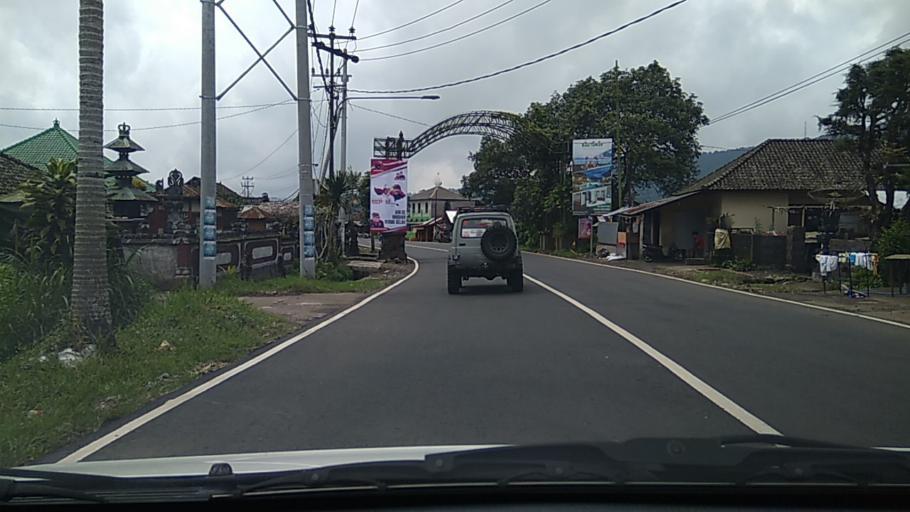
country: ID
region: Bali
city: Munduk
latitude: -8.2565
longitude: 115.1611
